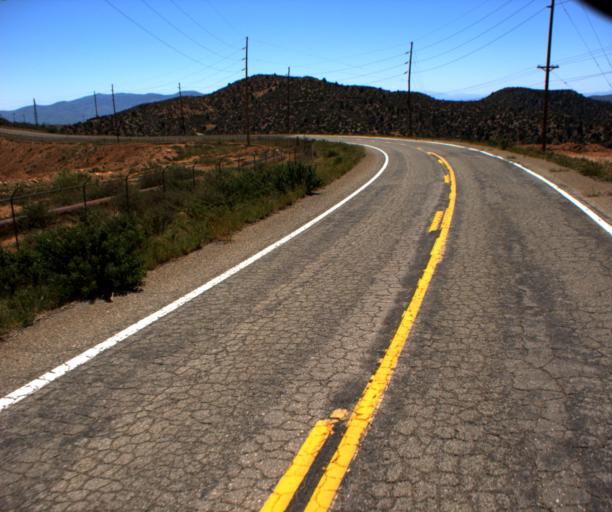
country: US
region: Arizona
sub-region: Greenlee County
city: Morenci
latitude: 33.0772
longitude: -109.3808
